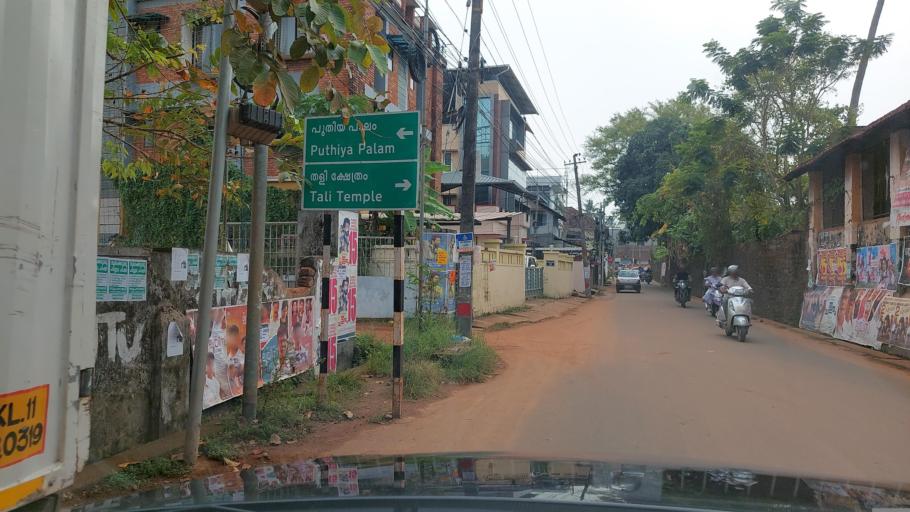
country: IN
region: Kerala
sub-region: Kozhikode
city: Kozhikode
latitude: 11.2487
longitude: 75.7888
